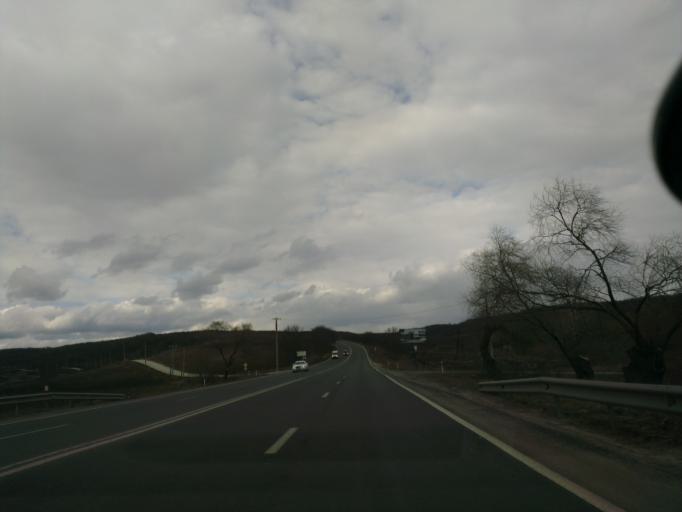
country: MD
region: Laloveni
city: Ialoveni
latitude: 46.9279
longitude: 28.6983
